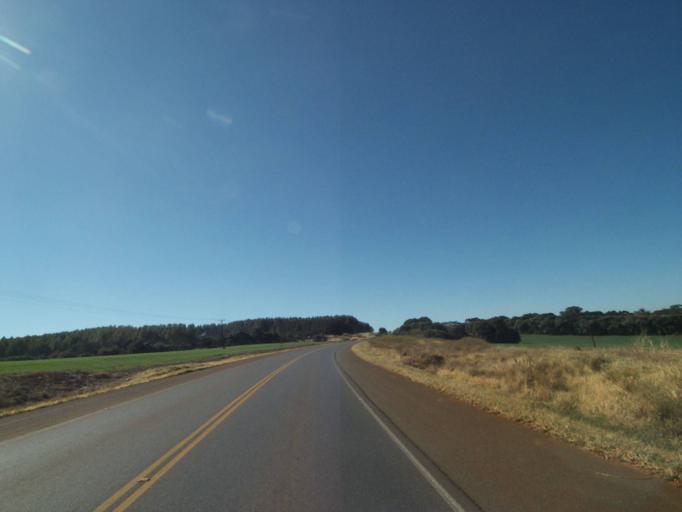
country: BR
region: Parana
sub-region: Tibagi
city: Tibagi
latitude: -24.4375
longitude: -50.4215
